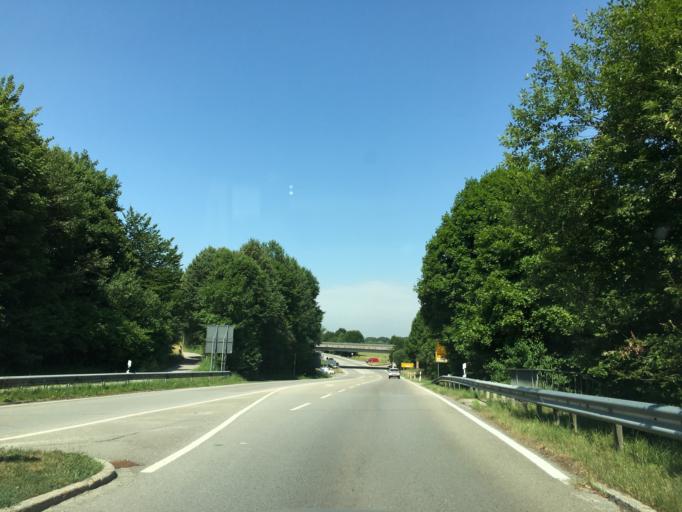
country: DE
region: Bavaria
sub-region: Upper Bavaria
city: Wasserburg am Inn
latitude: 48.0630
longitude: 12.2026
